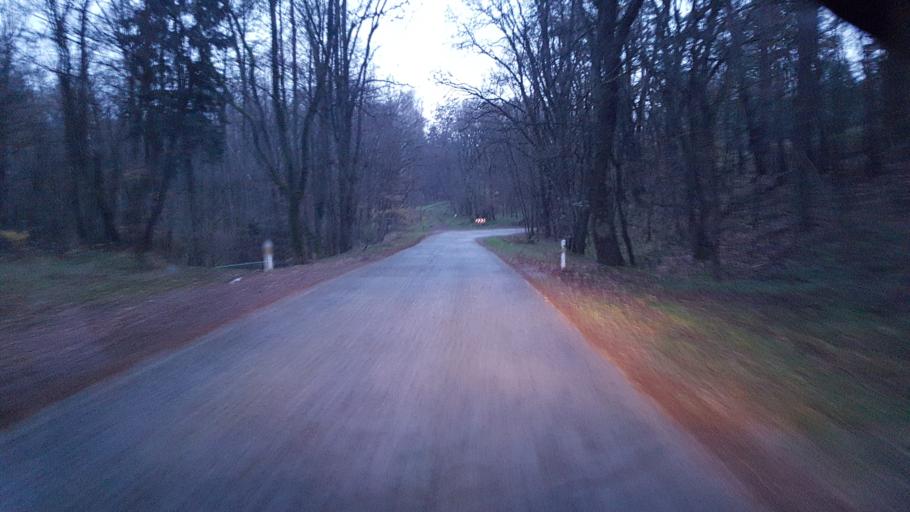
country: DE
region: Brandenburg
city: Jamlitz
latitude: 51.9980
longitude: 14.3700
